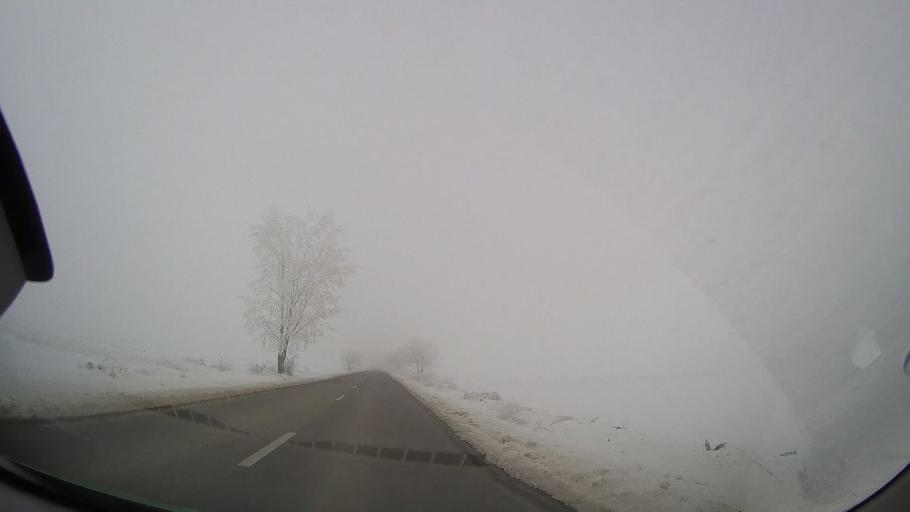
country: RO
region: Iasi
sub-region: Comuna Mogosesti-Siret
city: Mogosesti-Siret
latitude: 47.1477
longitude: 26.7783
